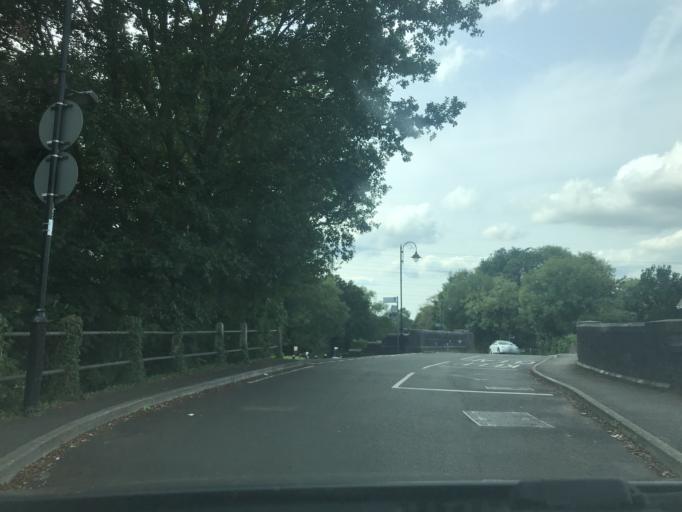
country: GB
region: England
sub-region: Surrey
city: Weybridge
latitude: 51.3715
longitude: -0.4658
